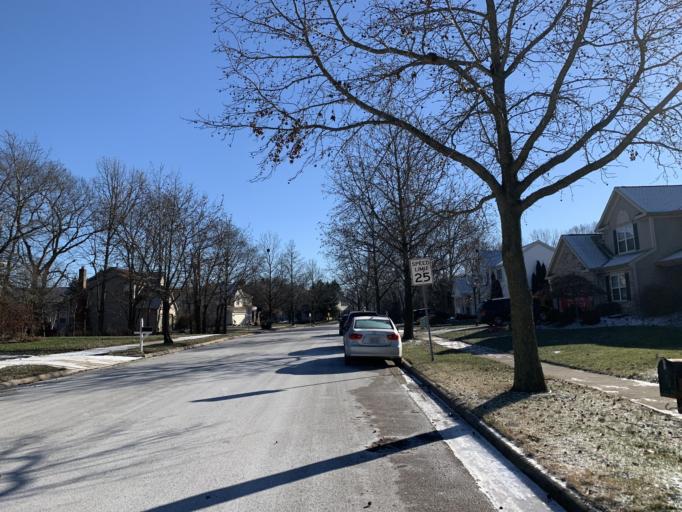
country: US
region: Ohio
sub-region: Franklin County
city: Dublin
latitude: 40.1251
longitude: -83.1653
